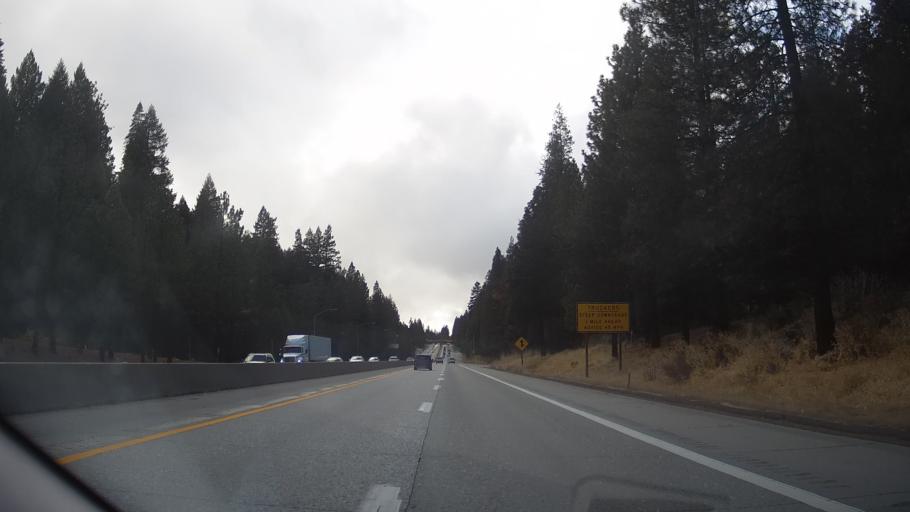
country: US
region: California
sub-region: Placer County
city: Foresthill
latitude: 39.2141
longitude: -120.7779
